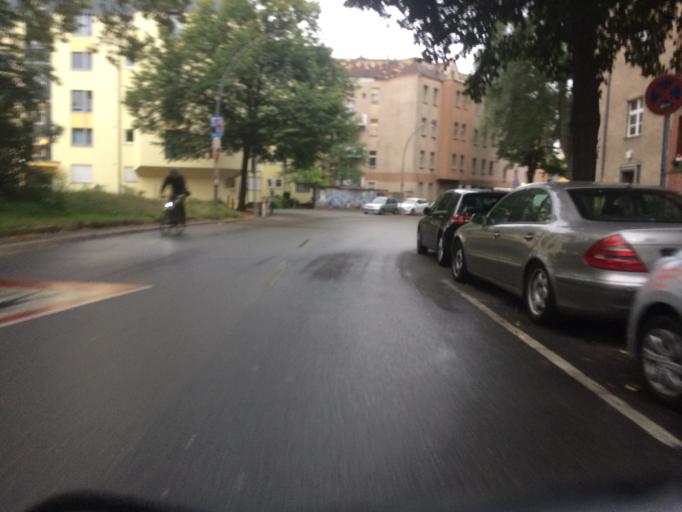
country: DE
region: Berlin
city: Gesundbrunnen
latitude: 52.5632
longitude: 13.3738
